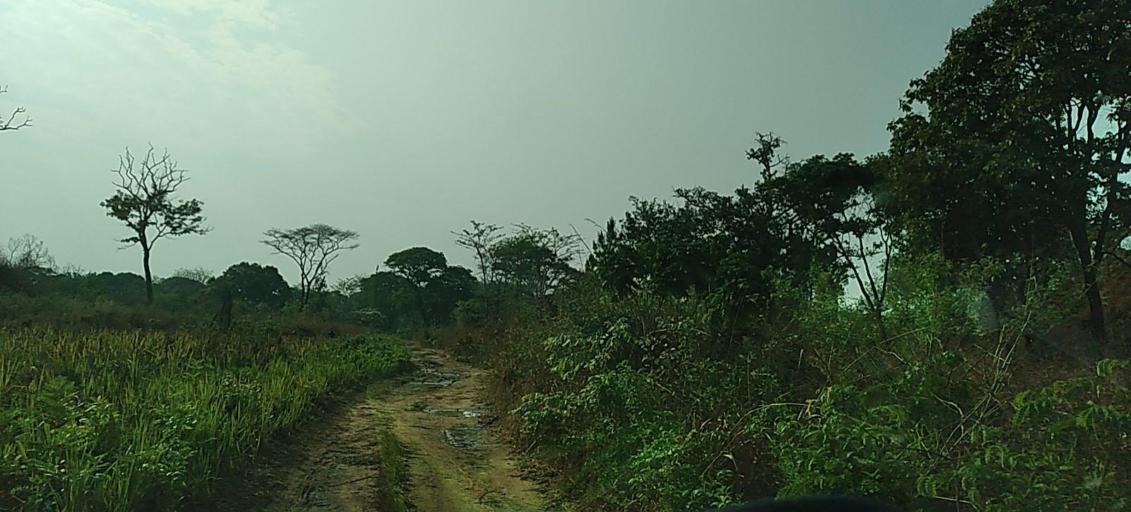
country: ZM
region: North-Western
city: Solwezi
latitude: -12.3897
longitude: 26.5727
